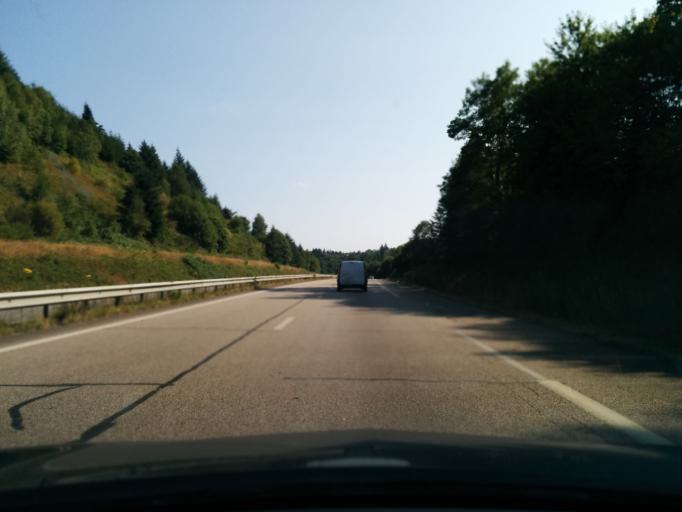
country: FR
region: Limousin
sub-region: Departement de la Haute-Vienne
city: Bonnac-la-Cote
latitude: 45.9681
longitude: 1.3203
